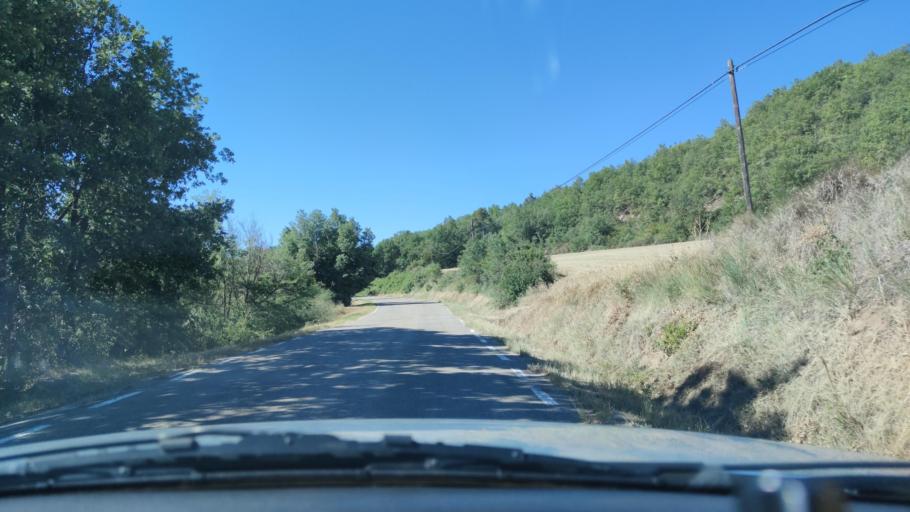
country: ES
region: Catalonia
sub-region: Provincia de Lleida
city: Solsona
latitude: 41.9613
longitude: 1.4932
